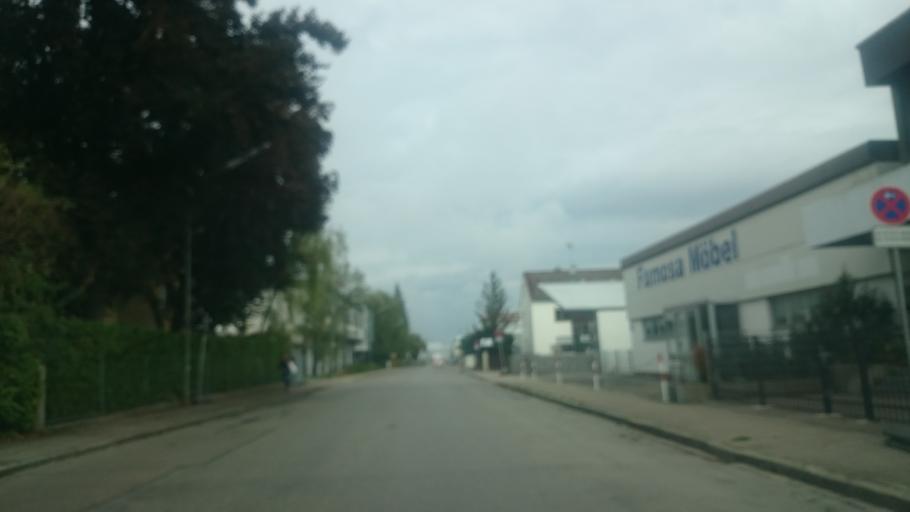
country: DE
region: Bavaria
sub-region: Swabia
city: Augsburg
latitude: 48.3759
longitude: 10.9367
